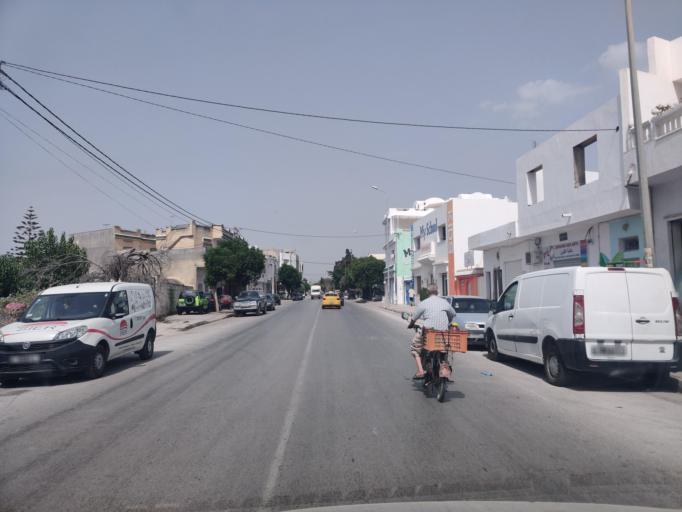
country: TN
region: Nabul
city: Al Hammamat
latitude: 36.4088
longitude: 10.6061
